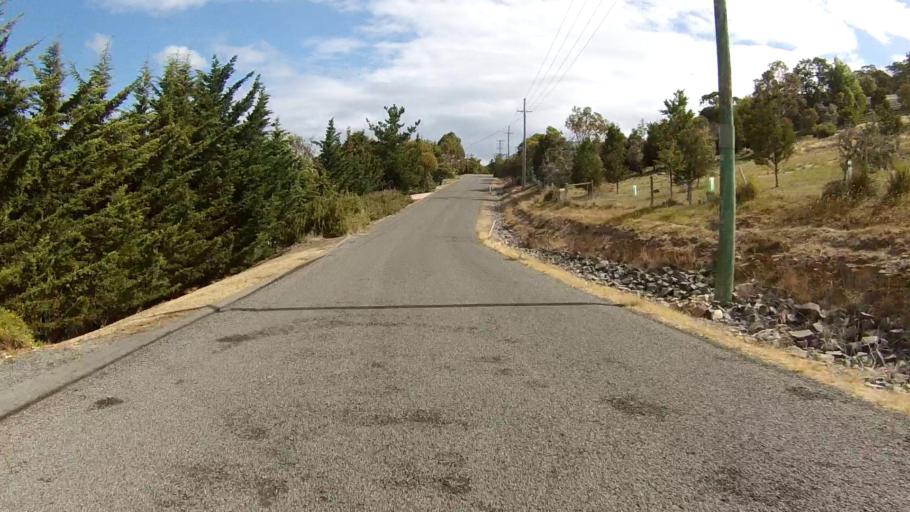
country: AU
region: Tasmania
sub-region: Clarence
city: Acton Park
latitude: -42.8823
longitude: 147.5038
